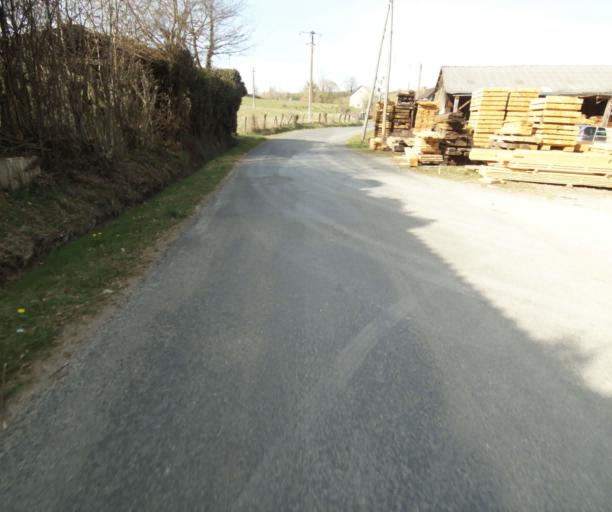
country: FR
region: Limousin
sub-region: Departement de la Correze
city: Naves
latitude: 45.3132
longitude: 1.7255
